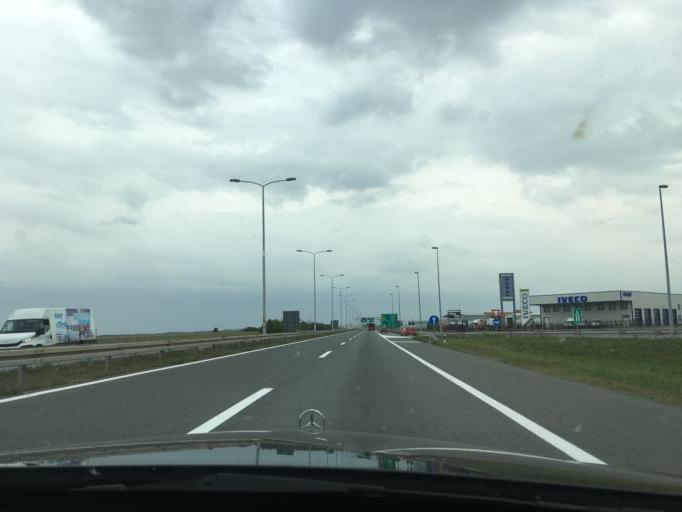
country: RS
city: Dobanovci
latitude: 44.8434
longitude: 20.2148
